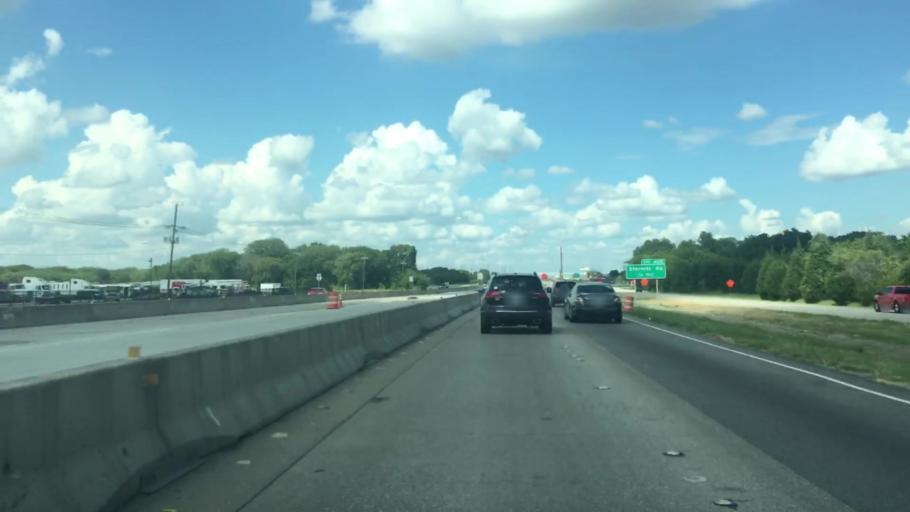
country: US
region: Texas
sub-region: Ellis County
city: Oak Leaf
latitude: 32.4654
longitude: -96.8413
